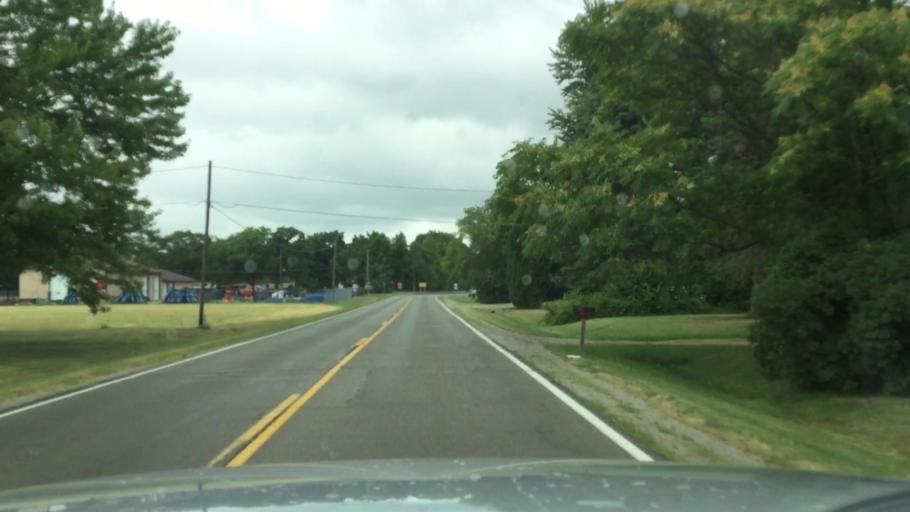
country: US
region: Michigan
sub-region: Genesee County
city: Clio
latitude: 43.1319
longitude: -83.7738
